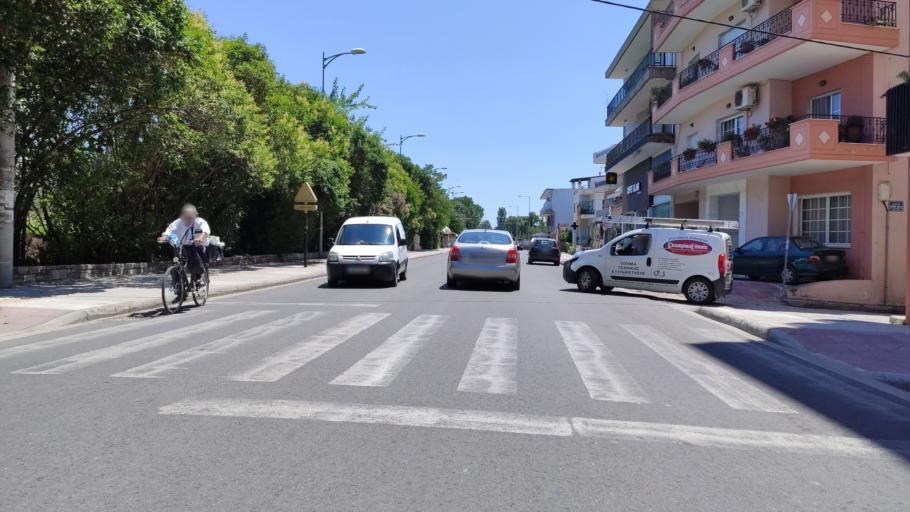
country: GR
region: East Macedonia and Thrace
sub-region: Nomos Rodopis
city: Komotini
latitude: 41.1133
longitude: 25.4107
